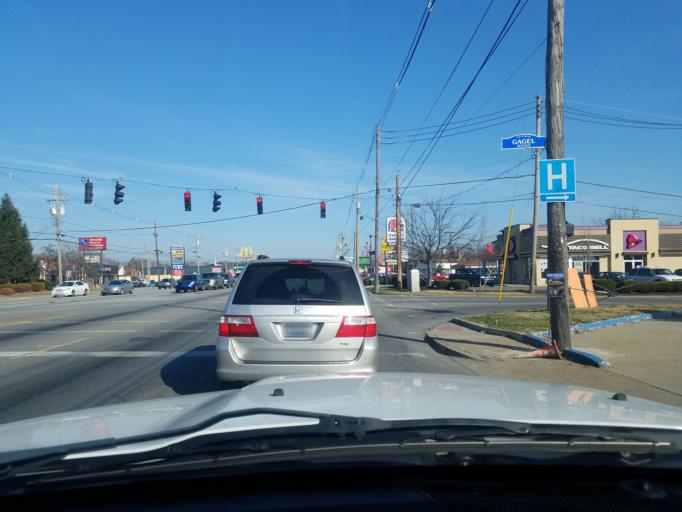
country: US
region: Kentucky
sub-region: Jefferson County
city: Shively
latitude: 38.1756
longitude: -85.8217
